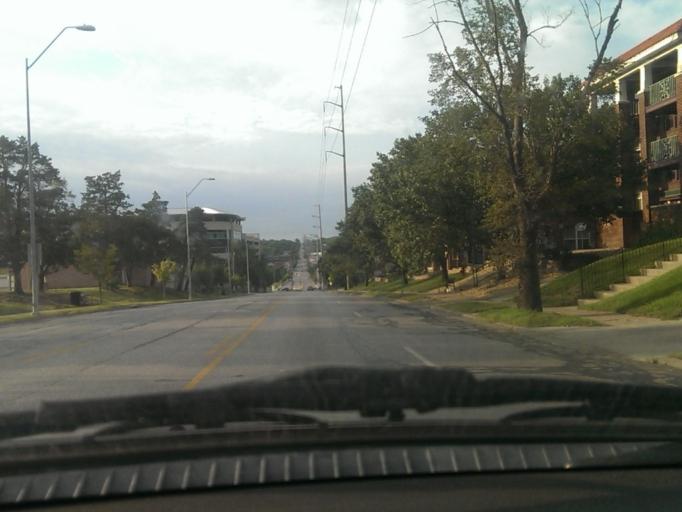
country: US
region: Kansas
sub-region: Johnson County
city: Westwood
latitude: 39.0348
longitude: -94.5733
